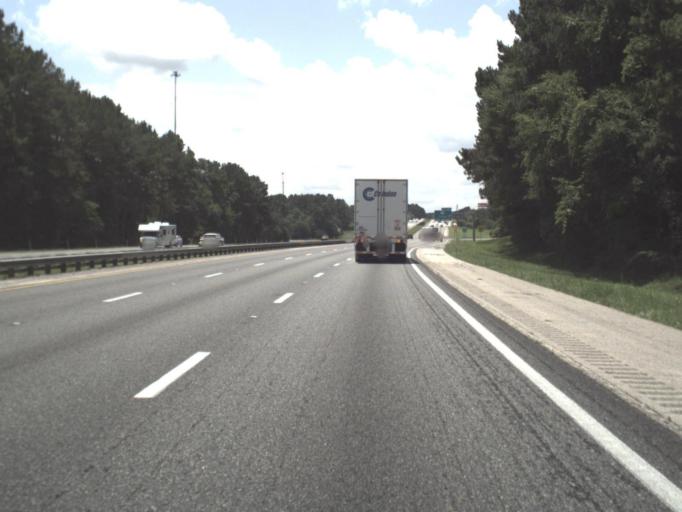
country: US
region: Florida
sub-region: Alachua County
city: High Springs
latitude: 29.8083
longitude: -82.5133
